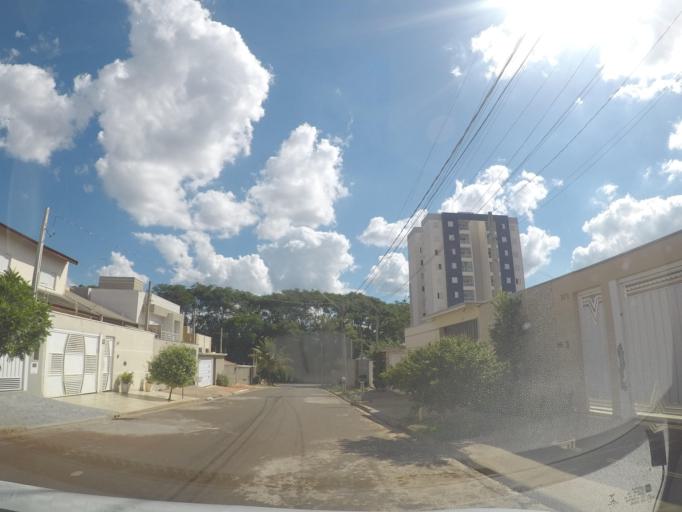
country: BR
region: Sao Paulo
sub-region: Sumare
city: Sumare
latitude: -22.8365
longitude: -47.2727
